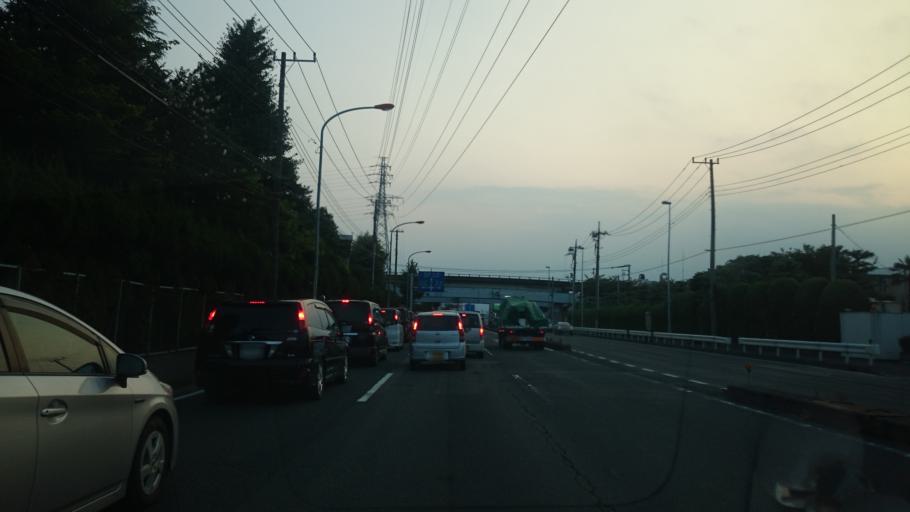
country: JP
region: Saitama
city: Ageoshimo
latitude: 35.9561
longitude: 139.6152
